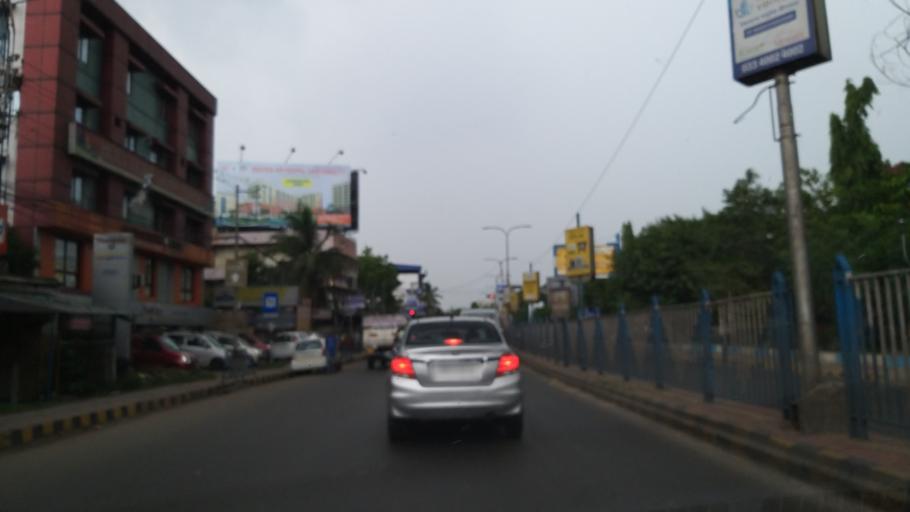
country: IN
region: West Bengal
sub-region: North 24 Parganas
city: Dam Dam
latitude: 22.6551
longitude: 88.4396
